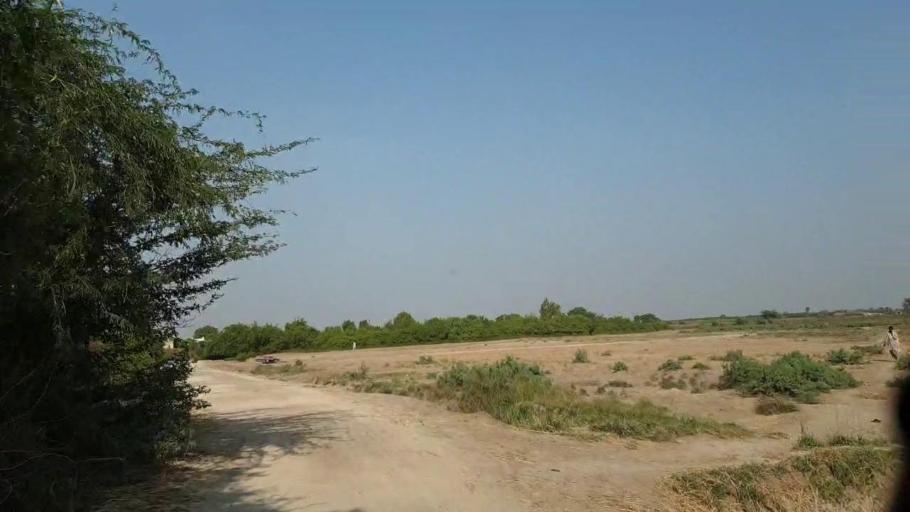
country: PK
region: Sindh
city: Bulri
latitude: 24.9448
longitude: 68.3876
